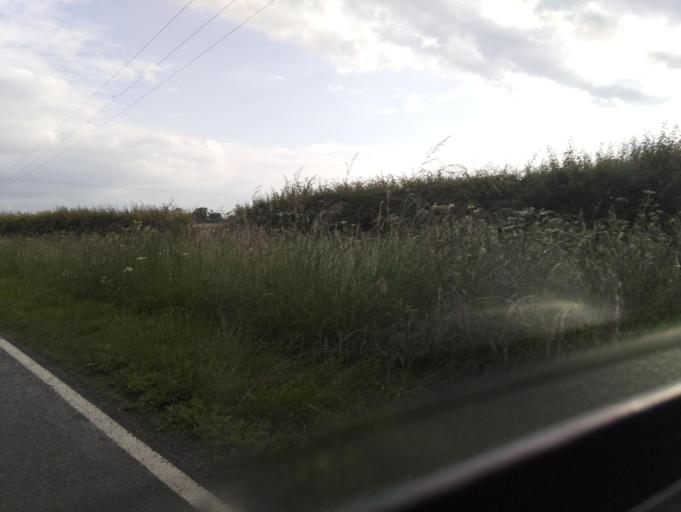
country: GB
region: England
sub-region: Lincolnshire
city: Great Gonerby
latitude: 53.0270
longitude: -0.6549
